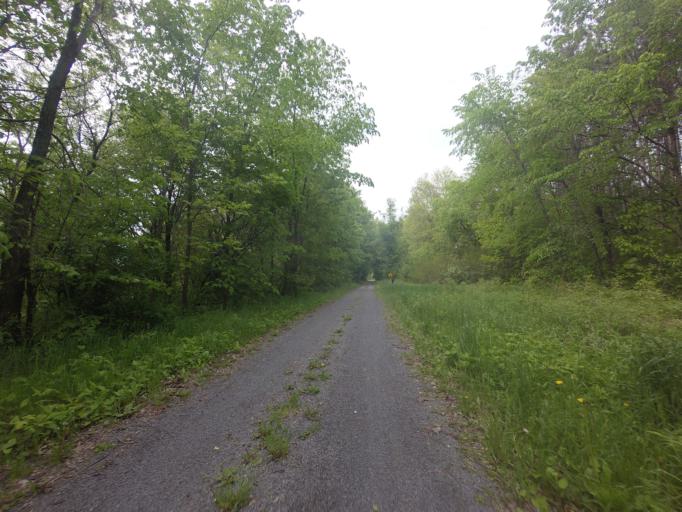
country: CA
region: Ontario
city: Kingston
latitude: 44.3630
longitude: -76.6272
